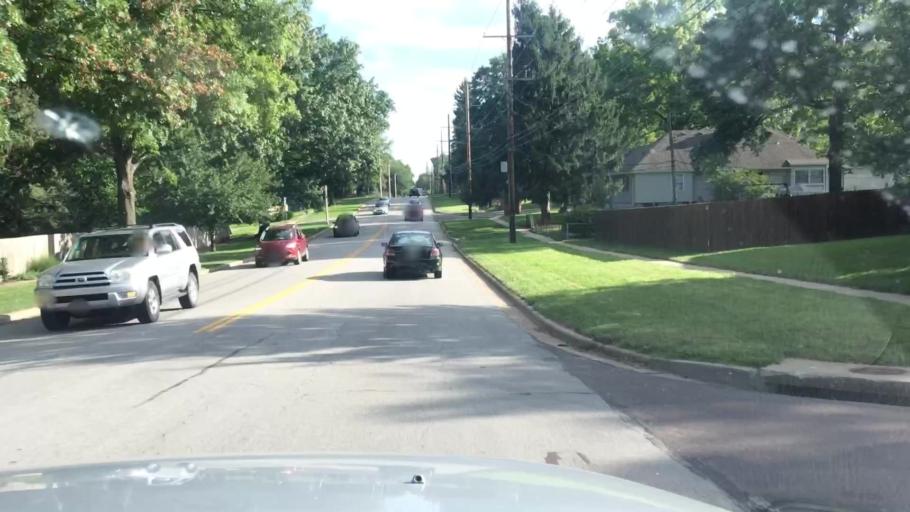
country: US
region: Kansas
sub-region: Johnson County
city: Prairie Village
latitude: 38.9768
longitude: -94.6490
